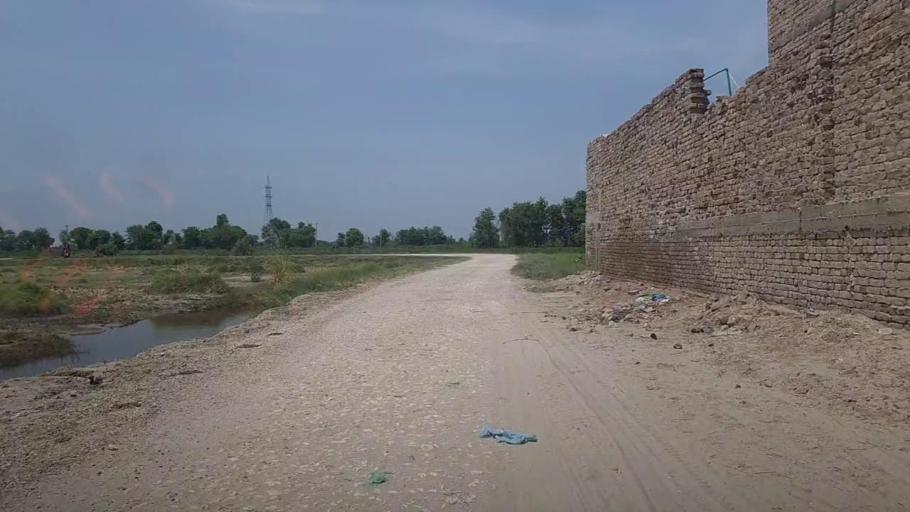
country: PK
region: Sindh
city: Ubauro
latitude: 28.1745
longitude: 69.7689
